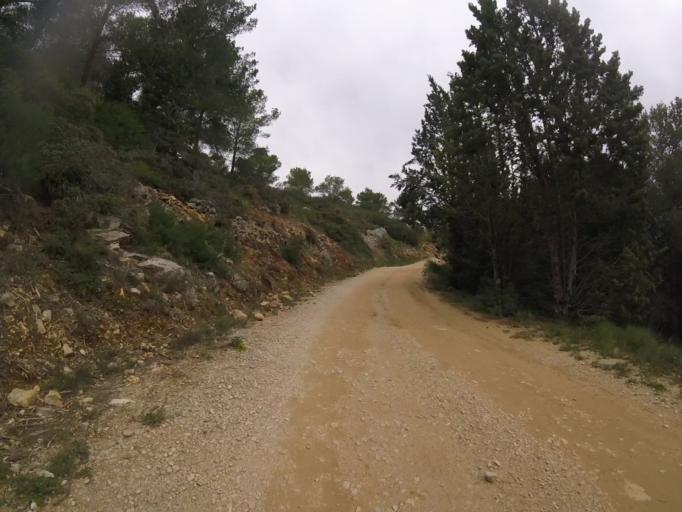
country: ES
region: Valencia
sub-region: Provincia de Castello
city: Alcala de Xivert
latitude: 40.3036
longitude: 0.2558
